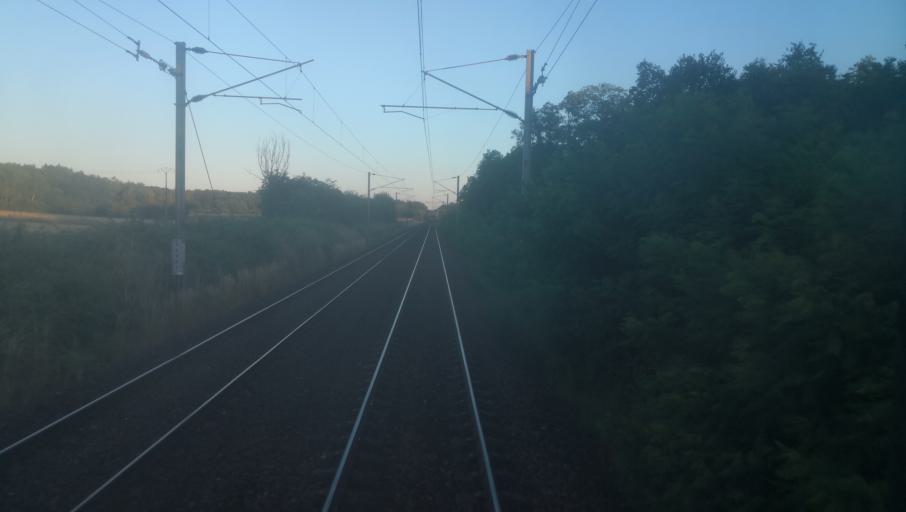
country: FR
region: Bourgogne
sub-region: Departement de la Nievre
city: La Charite-sur-Loire
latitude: 47.2352
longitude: 3.0105
